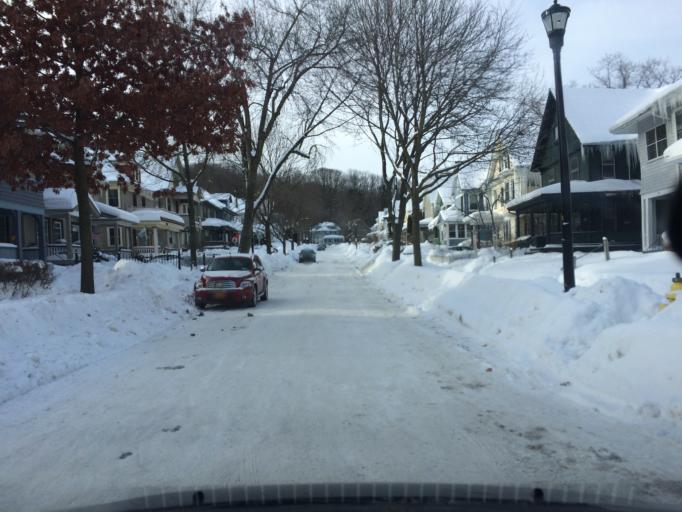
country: US
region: New York
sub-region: Monroe County
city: Rochester
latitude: 43.1378
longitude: -77.5878
